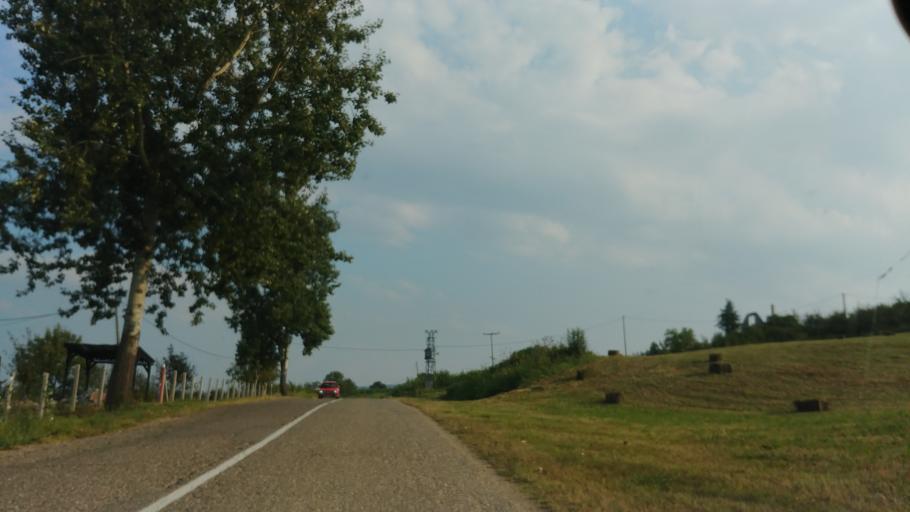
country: BA
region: Republika Srpska
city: Lopare
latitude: 44.7260
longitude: 18.8819
